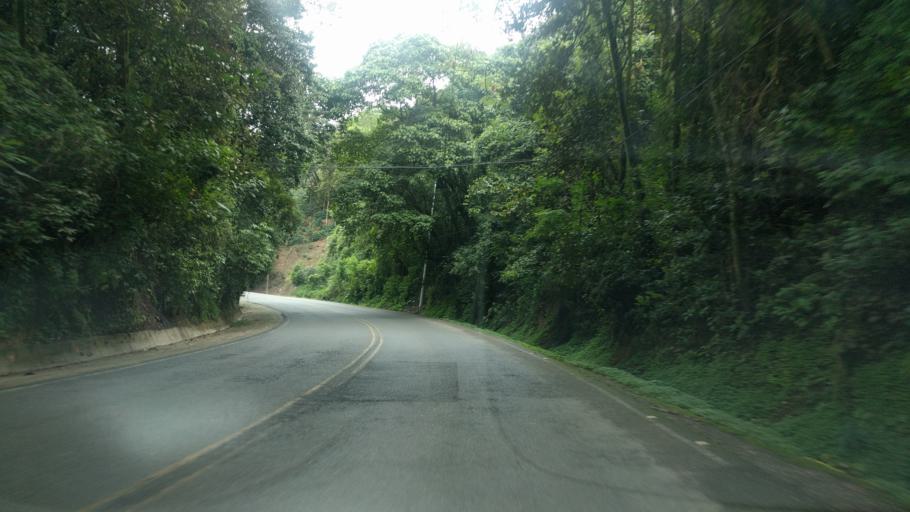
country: CR
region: Alajuela
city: San Rafael
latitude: 10.0330
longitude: -84.5082
